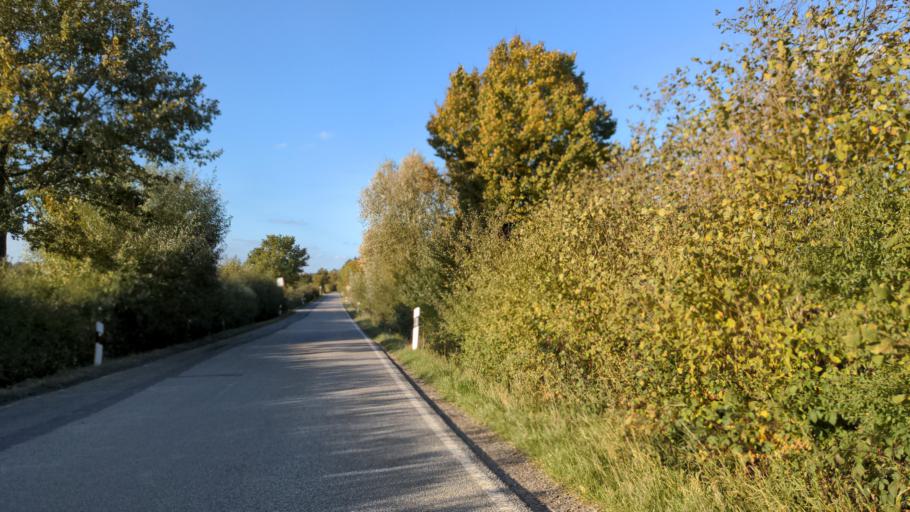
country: DE
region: Schleswig-Holstein
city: Monkhagen
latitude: 53.9400
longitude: 10.5335
